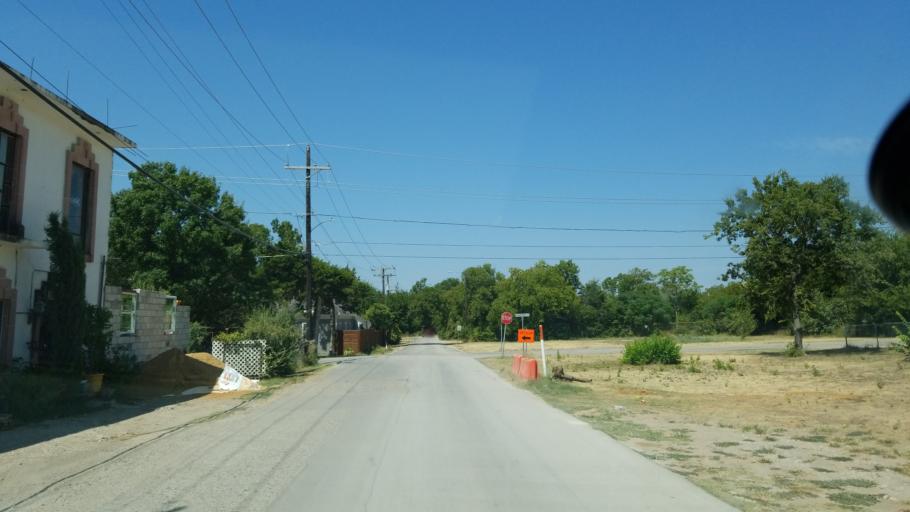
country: US
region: Texas
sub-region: Dallas County
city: Cockrell Hill
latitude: 32.7449
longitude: -96.8922
